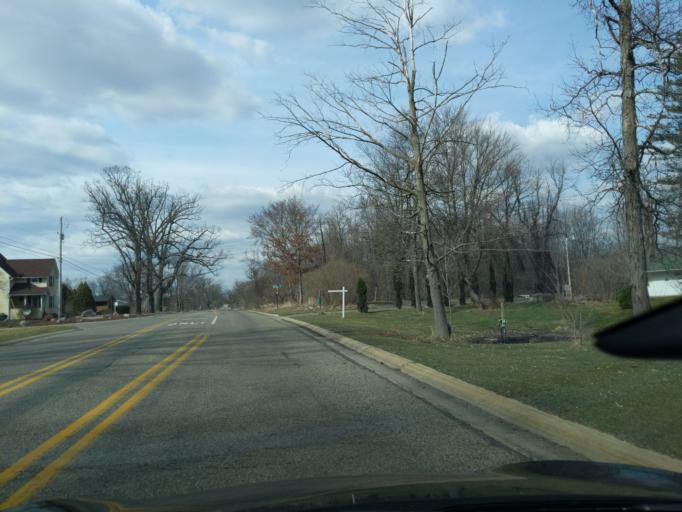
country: US
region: Michigan
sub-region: Jackson County
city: Jackson
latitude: 42.3270
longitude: -84.4136
